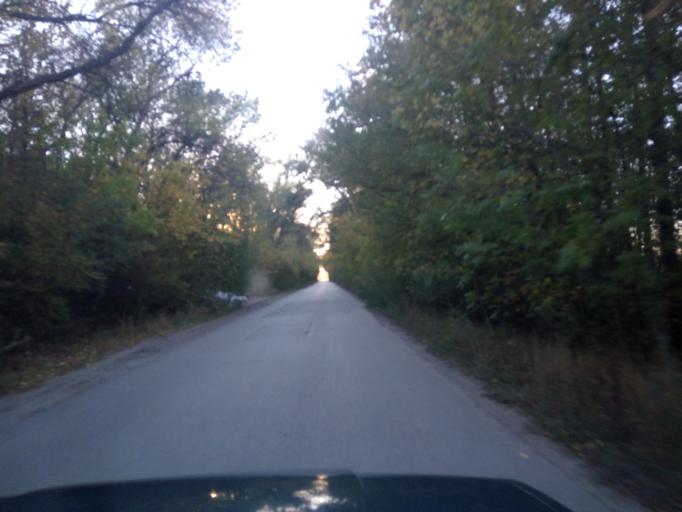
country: RU
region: Rostov
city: Temernik
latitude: 47.3553
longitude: 39.7349
